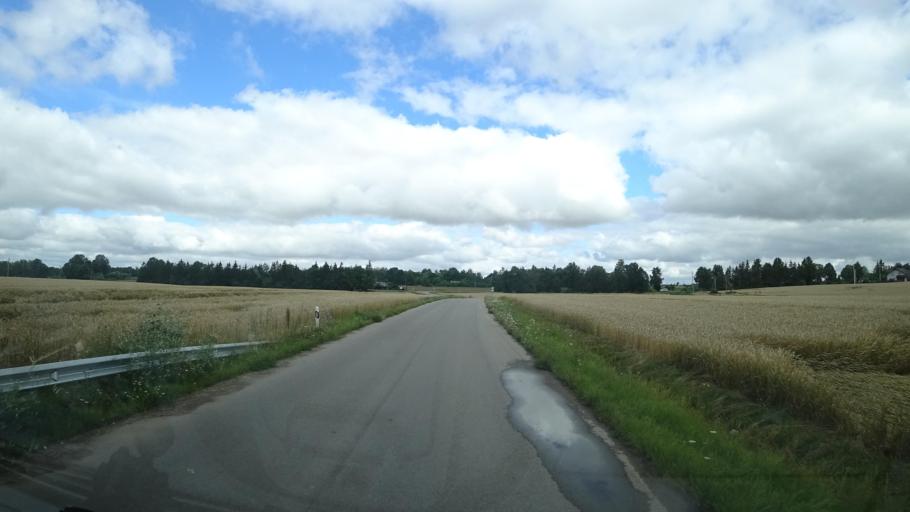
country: LT
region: Marijampoles apskritis
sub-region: Marijampole Municipality
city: Marijampole
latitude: 54.5193
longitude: 23.3213
